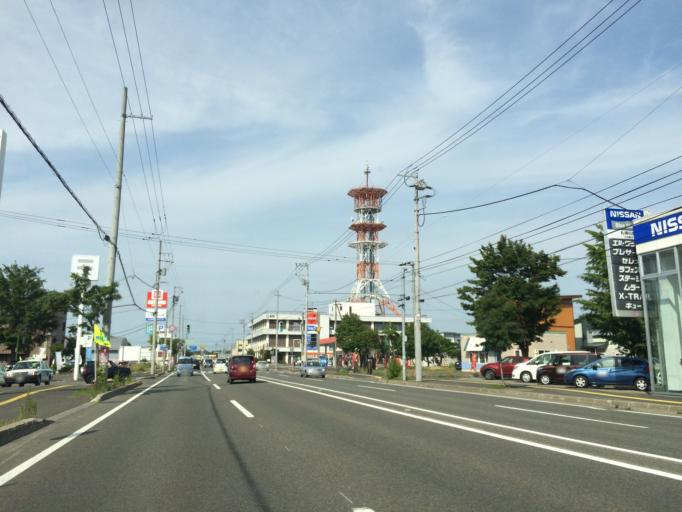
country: JP
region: Hokkaido
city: Ebetsu
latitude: 43.1090
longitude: 141.5462
